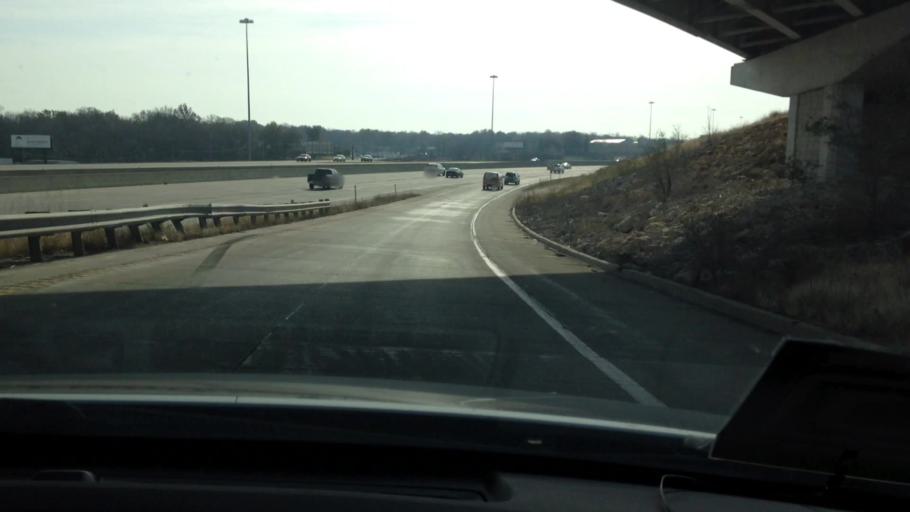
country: US
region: Missouri
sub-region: Jackson County
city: Grandview
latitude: 38.9312
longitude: -94.5285
